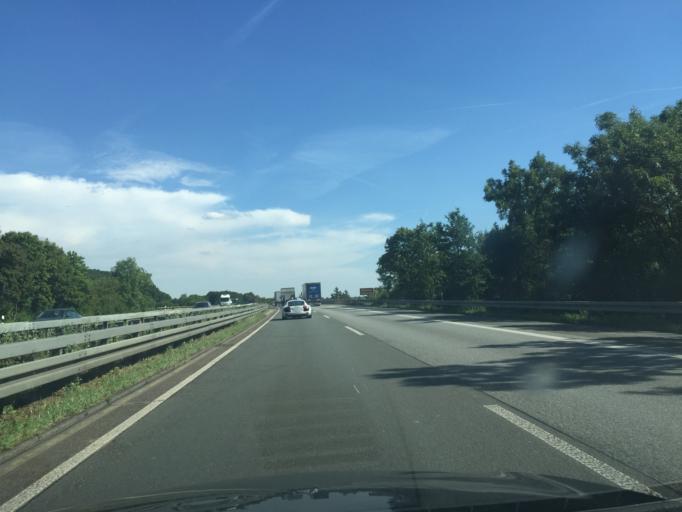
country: DE
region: Hesse
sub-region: Regierungsbezirk Giessen
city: Sinn
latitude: 50.6298
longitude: 8.3336
